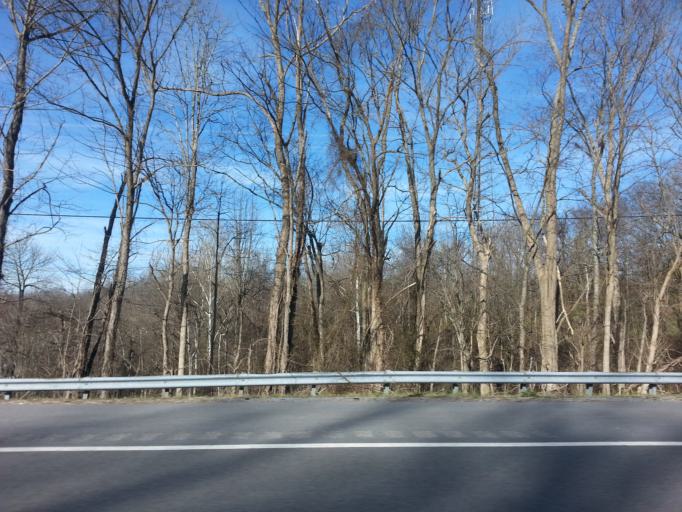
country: US
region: Tennessee
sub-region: Cannon County
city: Woodbury
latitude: 35.8012
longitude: -86.0025
